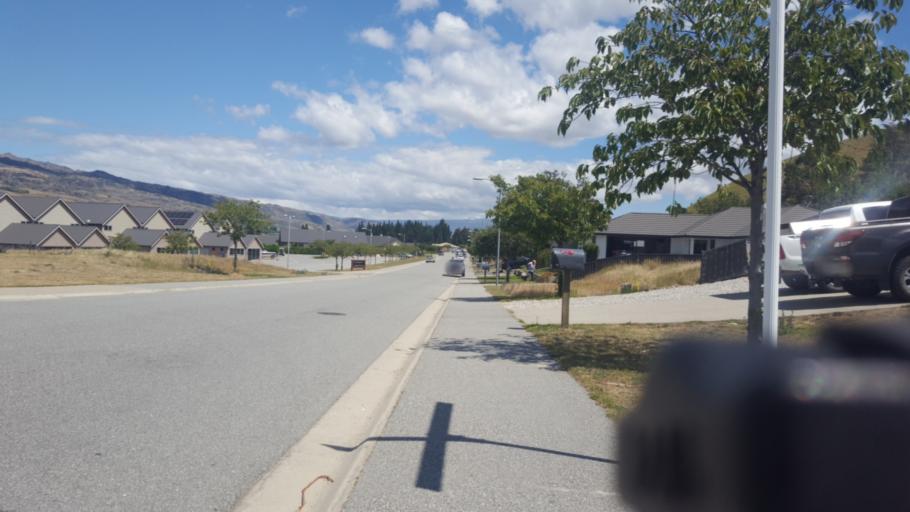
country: NZ
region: Otago
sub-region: Queenstown-Lakes District
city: Wanaka
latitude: -44.9788
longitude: 169.2360
